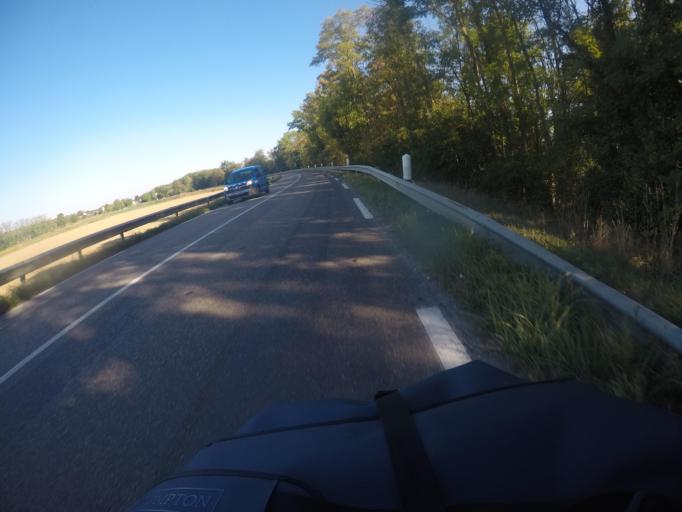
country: FR
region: Alsace
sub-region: Departement du Haut-Rhin
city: Rosenau
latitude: 47.6319
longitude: 7.5234
